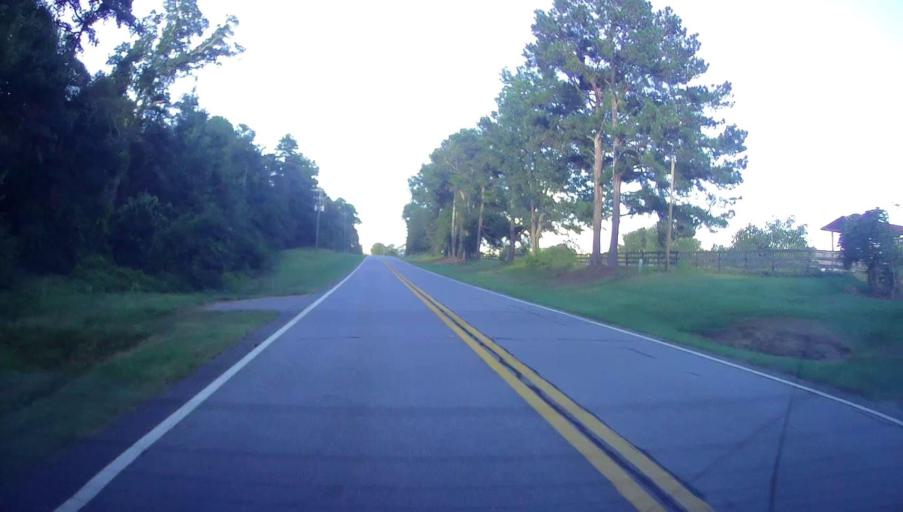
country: US
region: Georgia
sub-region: Pulaski County
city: Hawkinsville
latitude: 32.2663
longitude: -83.5162
